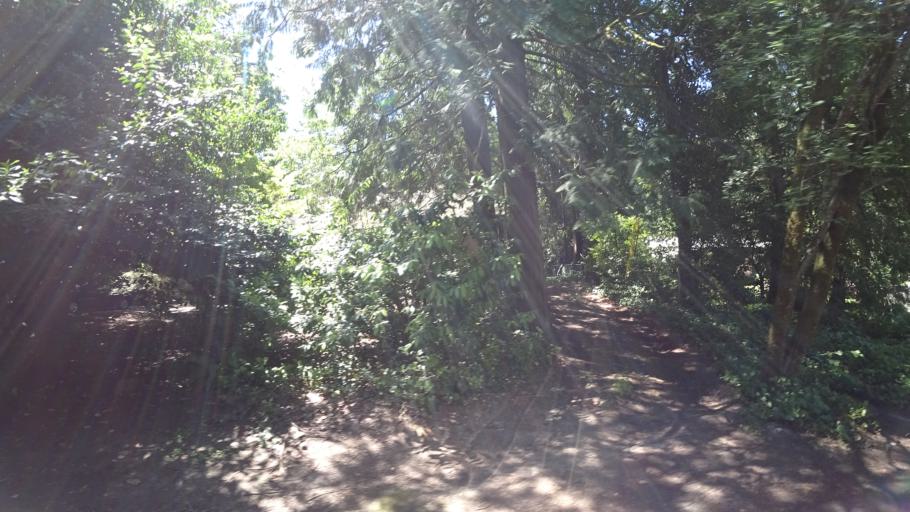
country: US
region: Oregon
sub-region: Washington County
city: Raleigh Hills
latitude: 45.4871
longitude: -122.7205
